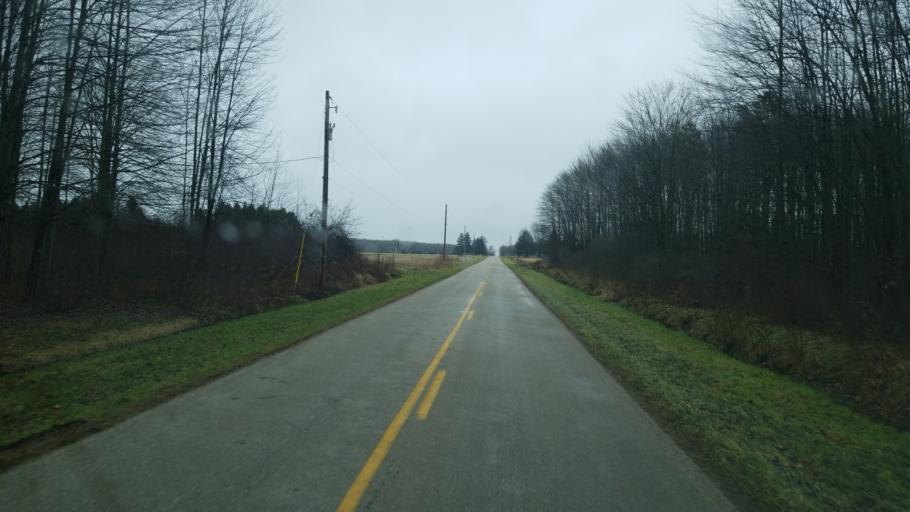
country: US
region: Ohio
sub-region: Ashtabula County
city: Roaming Shores
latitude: 41.5575
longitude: -80.7104
